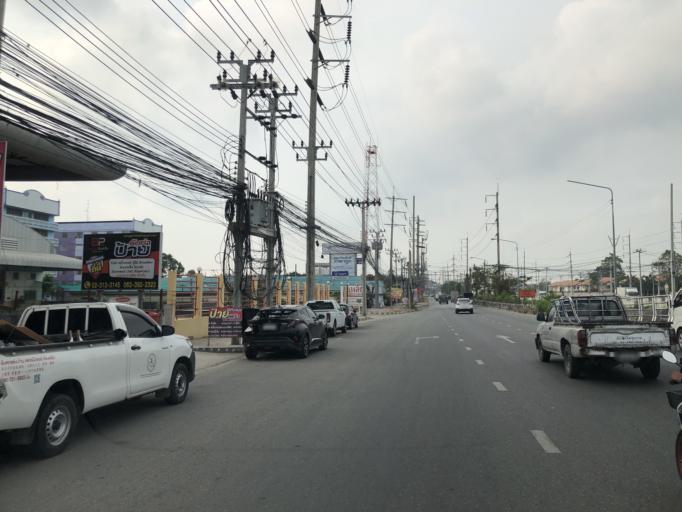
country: TH
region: Bangkok
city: Bang Na
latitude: 13.5914
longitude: 100.6990
